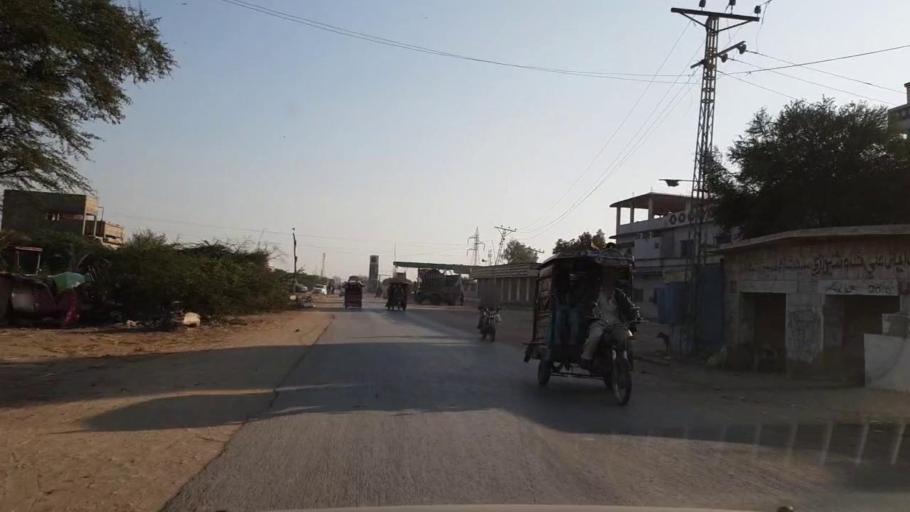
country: PK
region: Sindh
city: Mirpur Batoro
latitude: 24.7352
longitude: 68.2557
